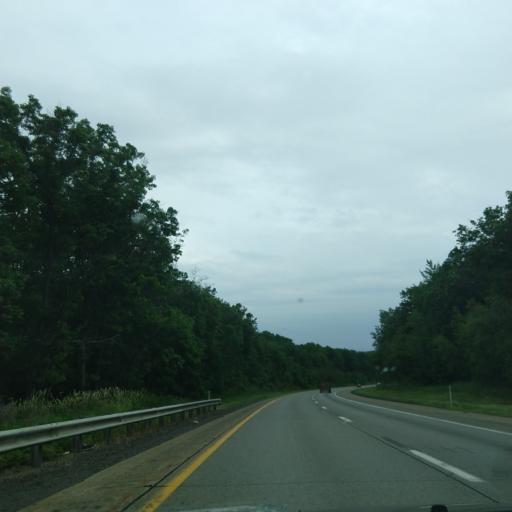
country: US
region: Pennsylvania
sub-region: Luzerne County
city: Nanticoke
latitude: 41.1622
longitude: -75.9558
